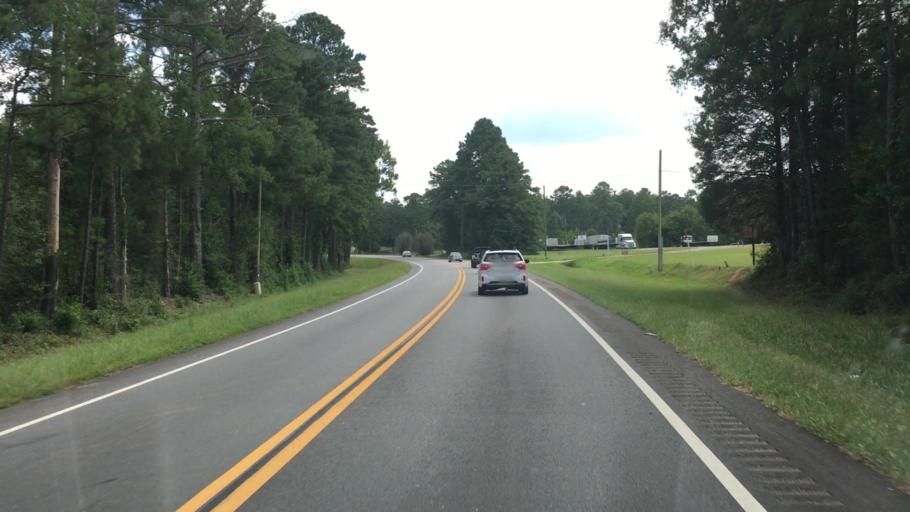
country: US
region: Georgia
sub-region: Putnam County
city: Eatonton
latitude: 33.3807
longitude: -83.3794
